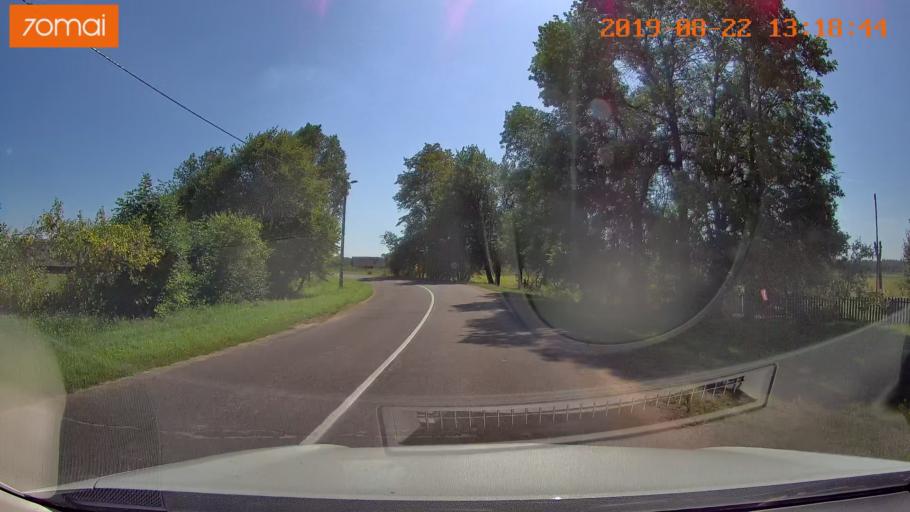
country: BY
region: Minsk
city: Urechcha
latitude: 53.2386
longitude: 27.9425
